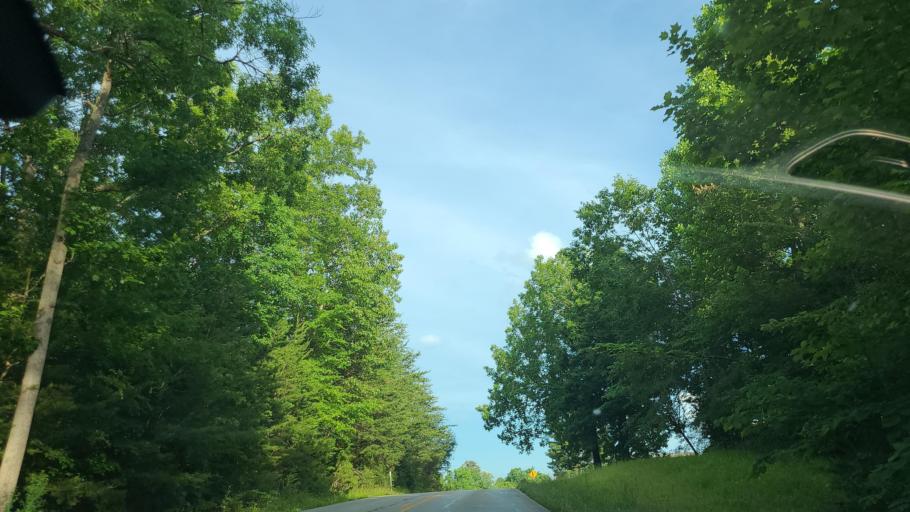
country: US
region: Kentucky
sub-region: Whitley County
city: Corbin
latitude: 36.8864
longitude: -84.2145
